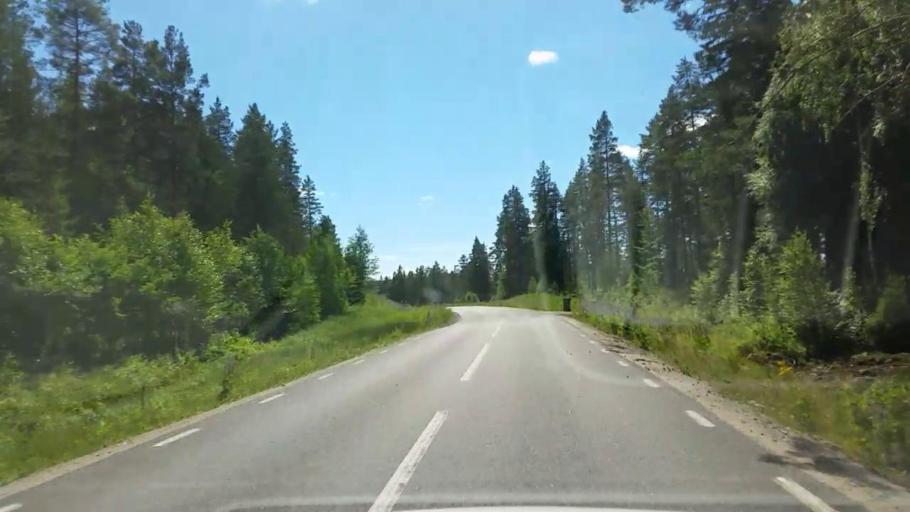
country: SE
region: Gaevleborg
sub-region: Ljusdals Kommun
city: Farila
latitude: 61.7344
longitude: 15.7269
